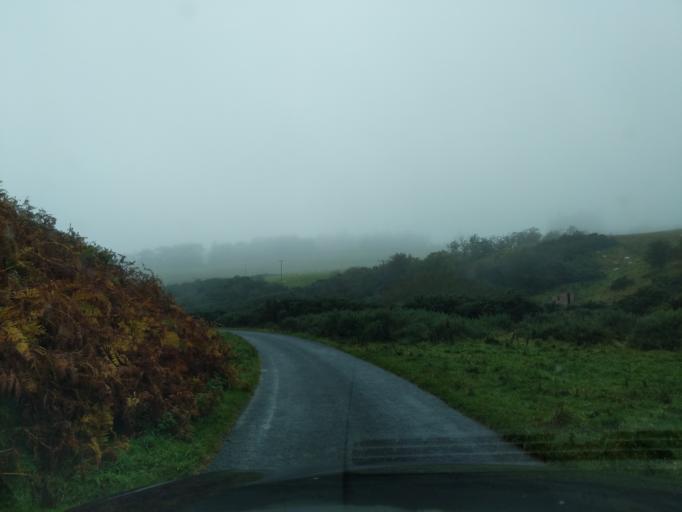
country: GB
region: Scotland
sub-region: East Lothian
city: Dunbar
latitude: 55.9306
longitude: -2.4236
